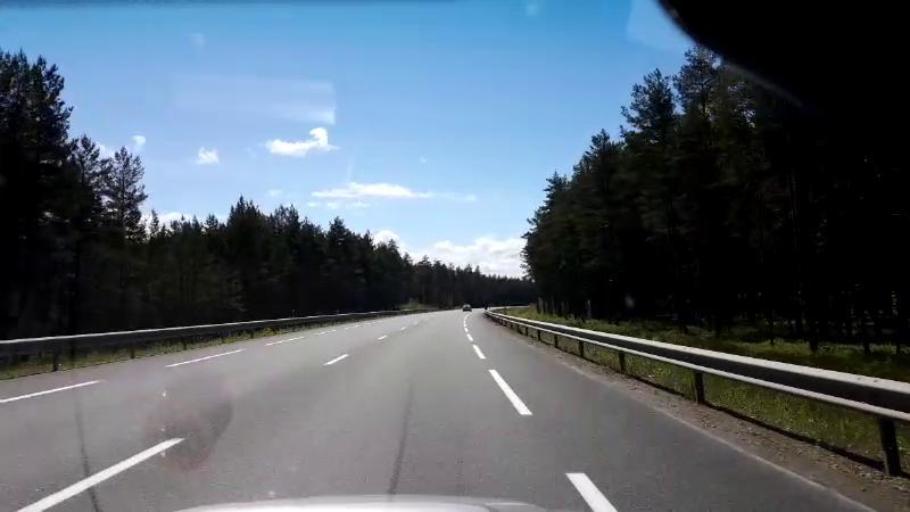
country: LV
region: Saulkrastu
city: Saulkrasti
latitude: 57.2328
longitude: 24.4260
